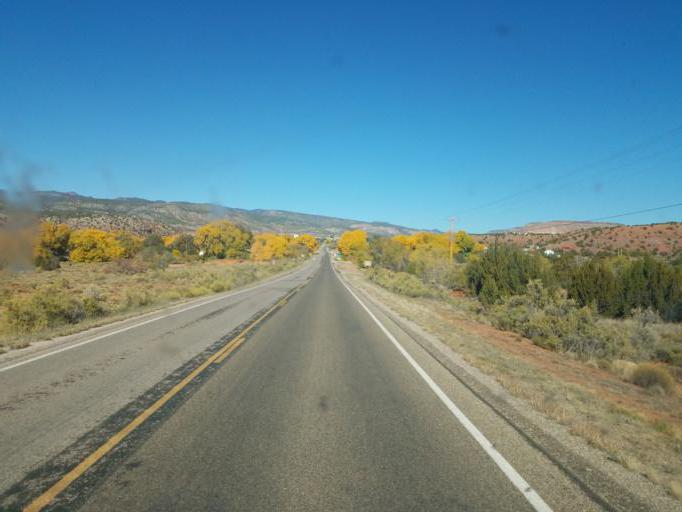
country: US
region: New Mexico
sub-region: Sandoval County
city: Jemez Pueblo
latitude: 35.6486
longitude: -106.7289
